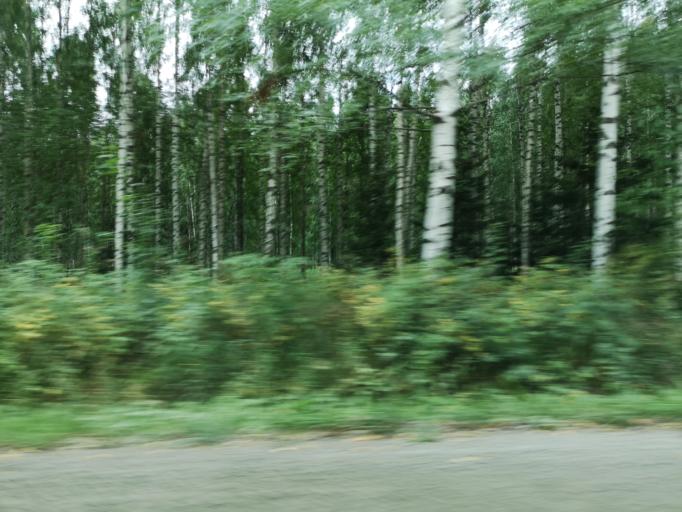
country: FI
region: Central Finland
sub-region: Jyvaeskylae
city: Hankasalmi
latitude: 62.4258
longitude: 26.6452
